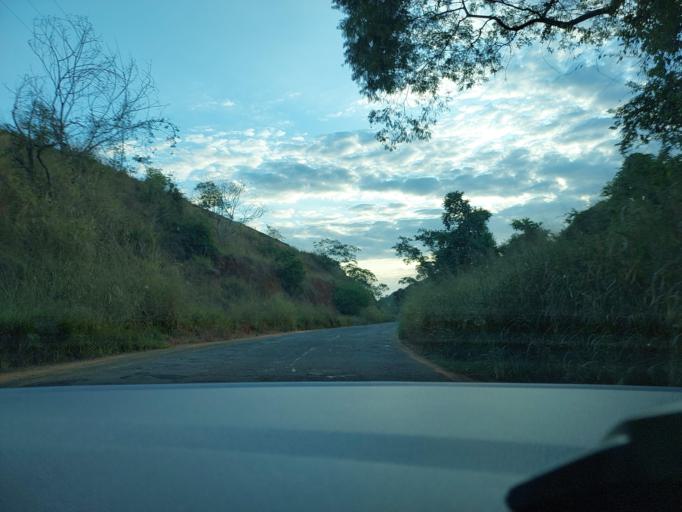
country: BR
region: Rio de Janeiro
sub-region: Natividade
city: Natividade
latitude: -21.1999
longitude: -42.1194
